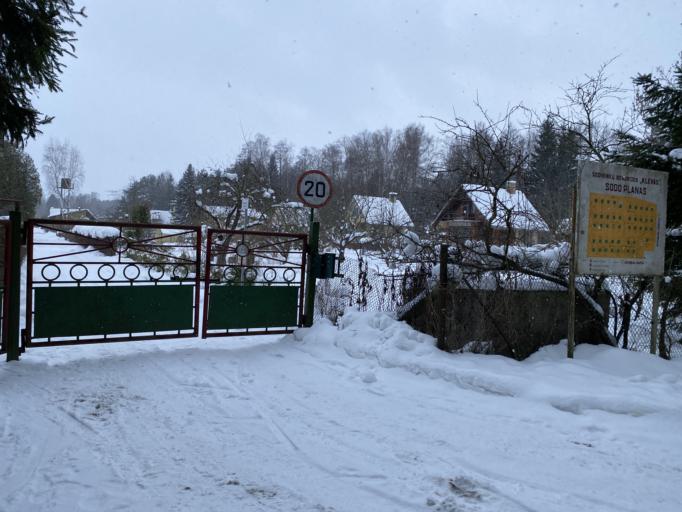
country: LT
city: Ramuciai
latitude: 54.8831
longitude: 24.0718
